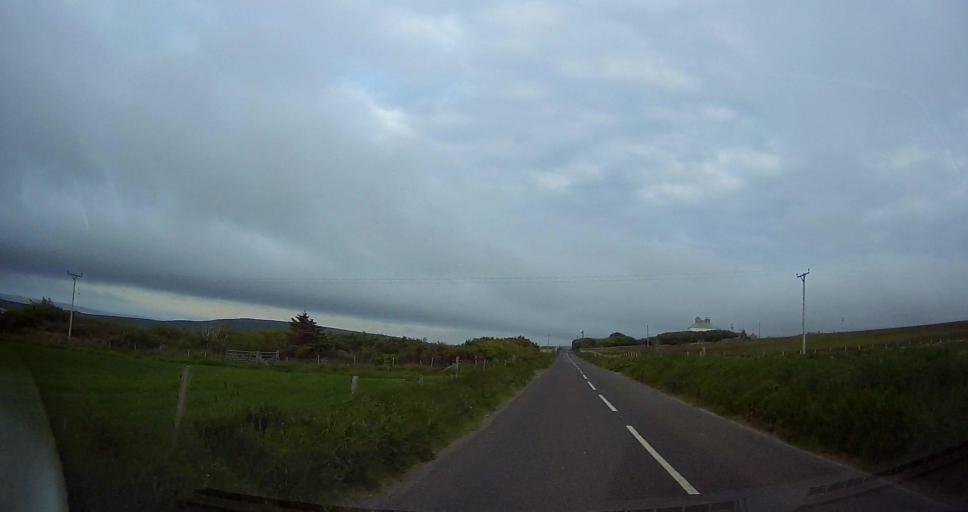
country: GB
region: Scotland
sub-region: Orkney Islands
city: Orkney
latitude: 59.1177
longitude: -3.1176
